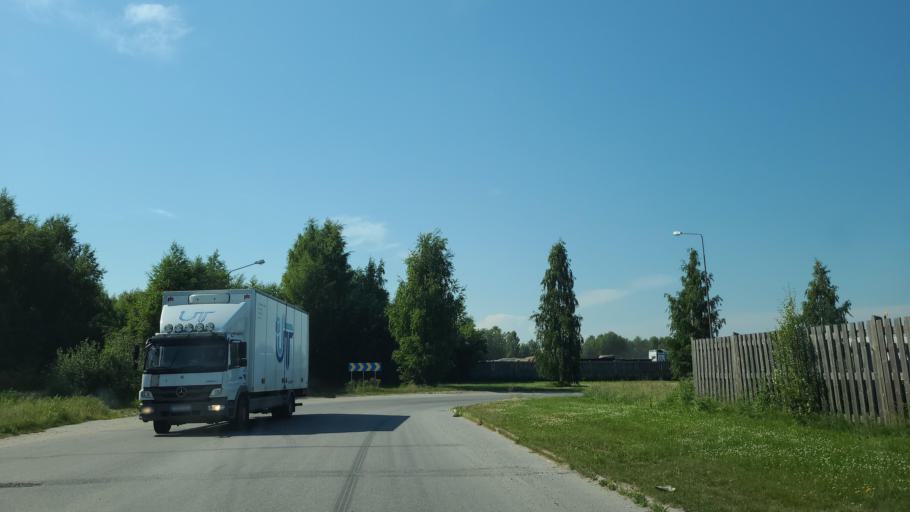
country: SE
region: Vaesterbotten
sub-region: Umea Kommun
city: Roback
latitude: 63.8448
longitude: 20.2120
